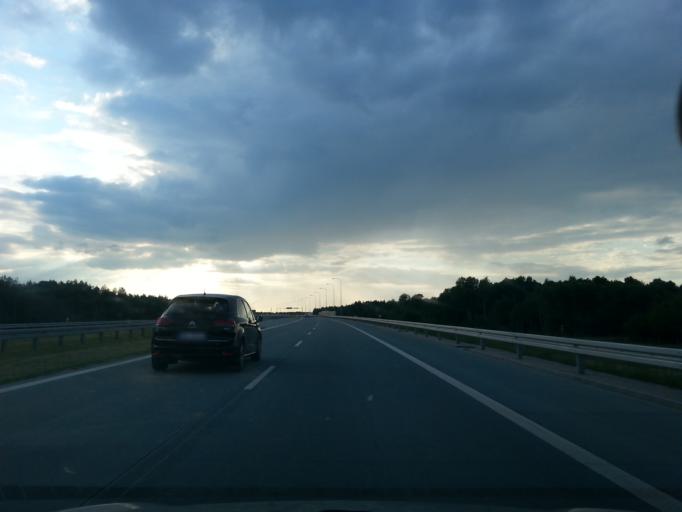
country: PL
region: Lodz Voivodeship
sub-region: Powiat zdunskowolski
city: Zapolice
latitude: 51.5941
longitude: 18.8856
